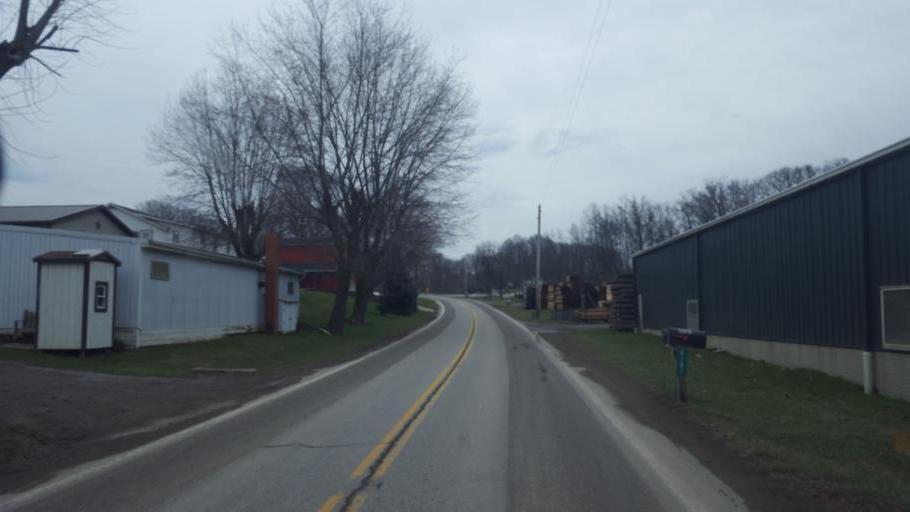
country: US
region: Ohio
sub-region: Tuscarawas County
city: Sugarcreek
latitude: 40.5001
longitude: -81.7760
